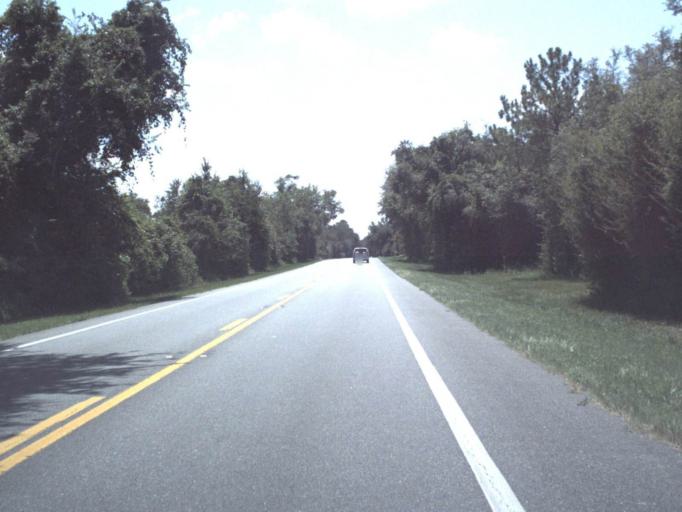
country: US
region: Florida
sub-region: Alachua County
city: Newberry
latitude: 29.6273
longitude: -82.6020
